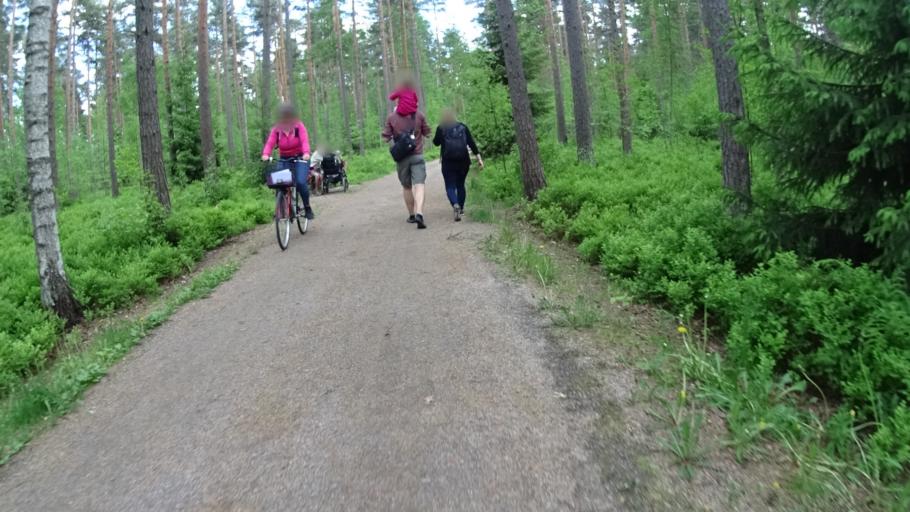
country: FI
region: Uusimaa
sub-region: Helsinki
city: Kilo
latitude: 60.1948
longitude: 24.7976
